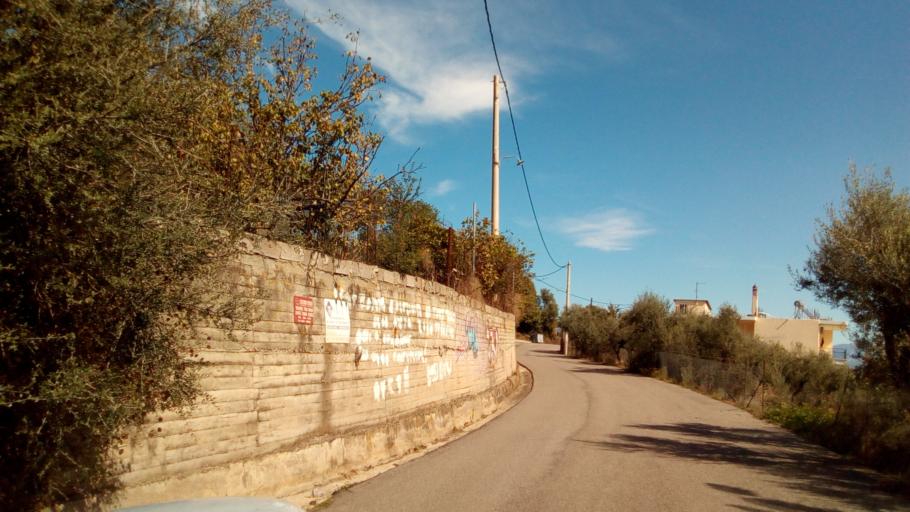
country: GR
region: West Greece
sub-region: Nomos Aitolias kai Akarnanias
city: Antirrio
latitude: 38.3597
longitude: 21.7529
